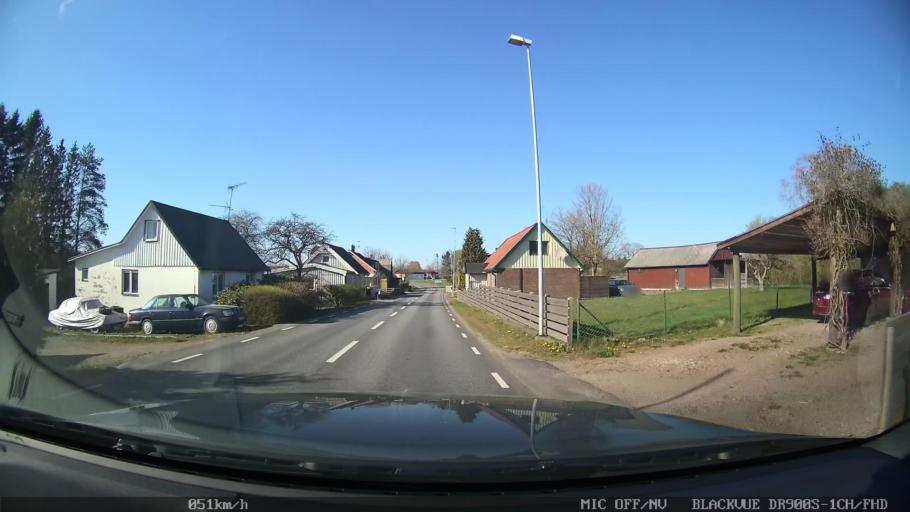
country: SE
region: Skane
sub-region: Bjuvs Kommun
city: Billesholm
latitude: 56.0520
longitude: 12.9981
